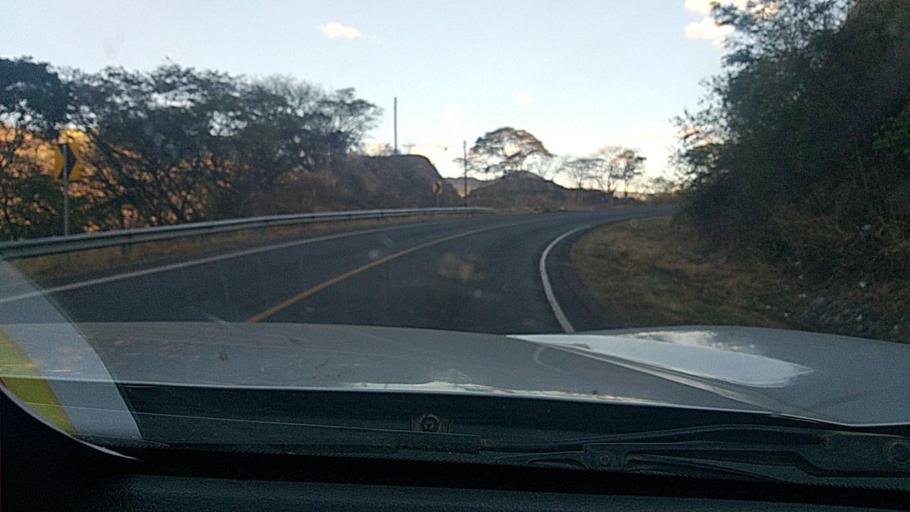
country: NI
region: Esteli
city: Condega
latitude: 13.2684
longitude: -86.3552
